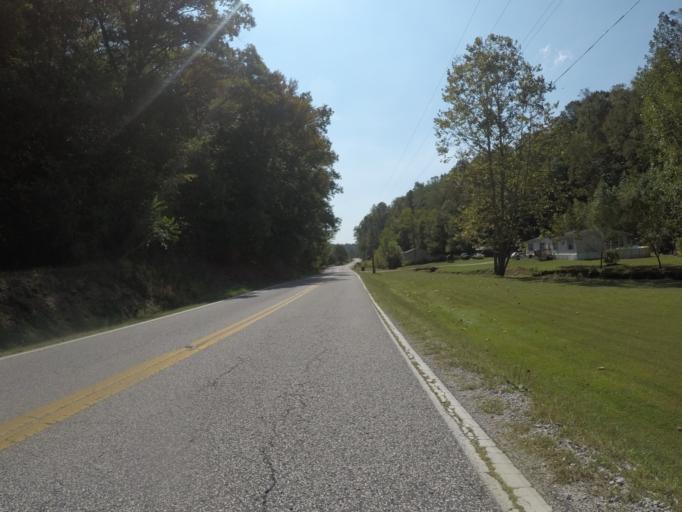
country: US
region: West Virginia
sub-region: Cabell County
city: Lesage
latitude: 38.5678
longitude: -82.3993
